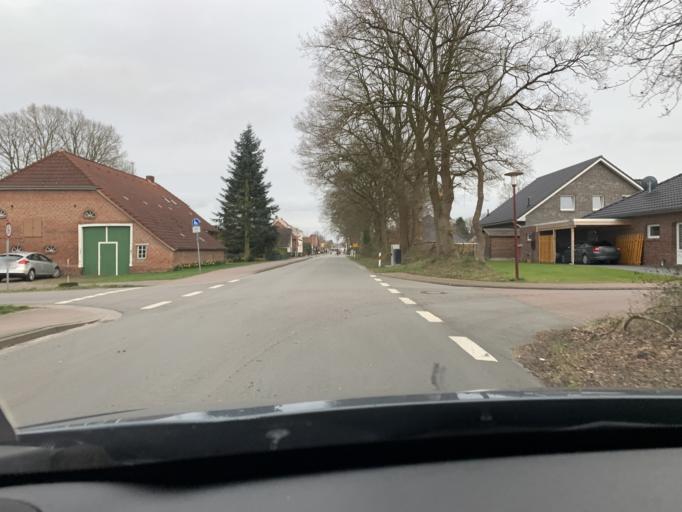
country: DE
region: Lower Saxony
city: Apen
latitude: 53.2245
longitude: 7.7513
